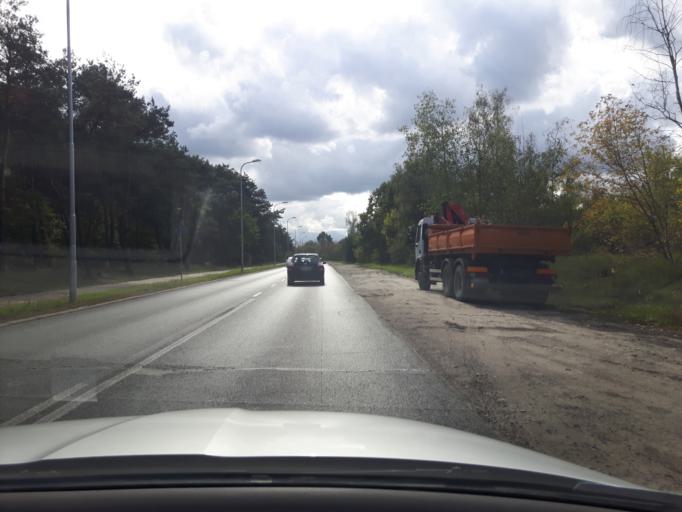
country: PL
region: Masovian Voivodeship
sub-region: Warszawa
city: Rembertow
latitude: 52.2325
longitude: 21.1437
